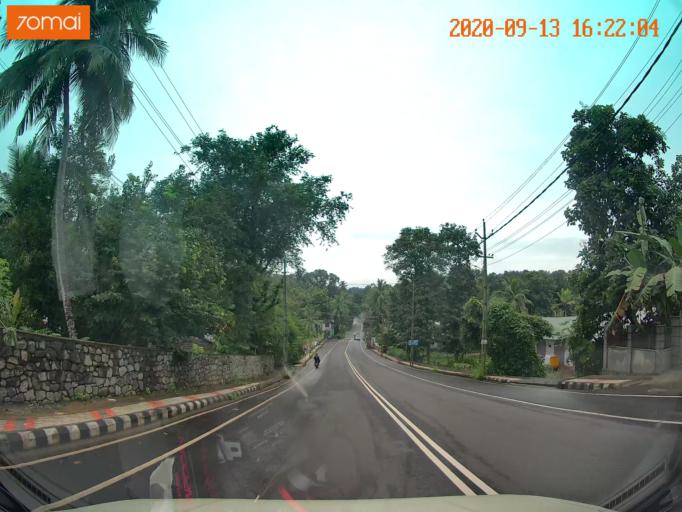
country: IN
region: Kerala
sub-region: Kottayam
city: Lalam
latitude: 9.7112
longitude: 76.6696
